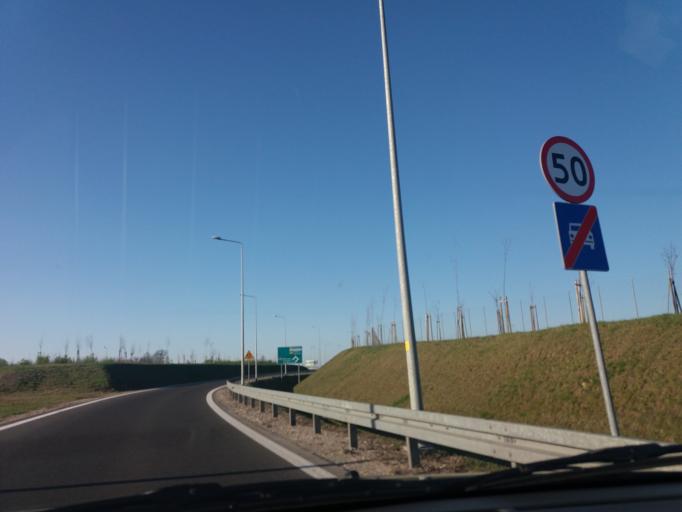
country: PL
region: Warmian-Masurian Voivodeship
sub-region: Powiat nidzicki
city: Nidzica
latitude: 53.3315
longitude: 20.4383
